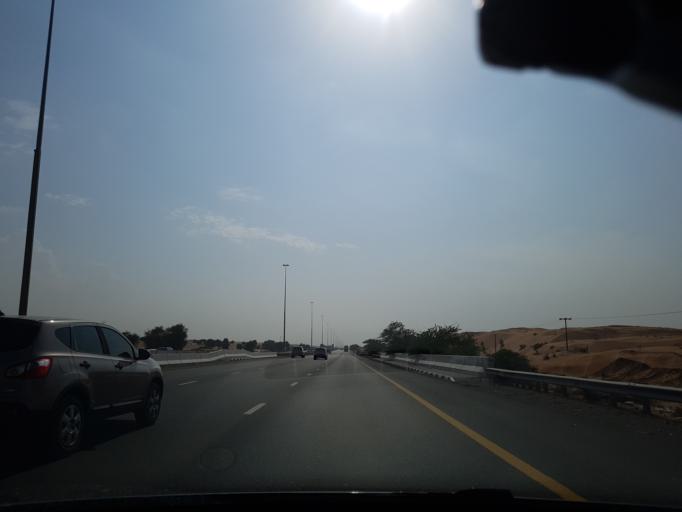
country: AE
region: Umm al Qaywayn
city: Umm al Qaywayn
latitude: 25.5118
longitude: 55.7043
